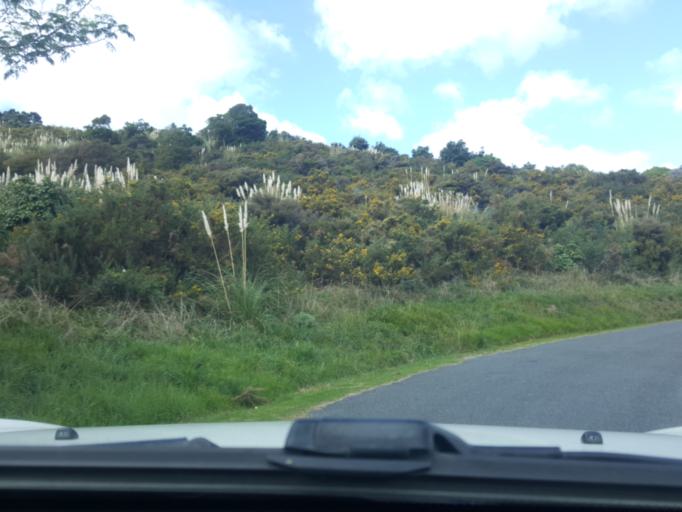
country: NZ
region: Bay of Plenty
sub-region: Western Bay of Plenty District
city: Waihi Beach
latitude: -37.4654
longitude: 175.9877
